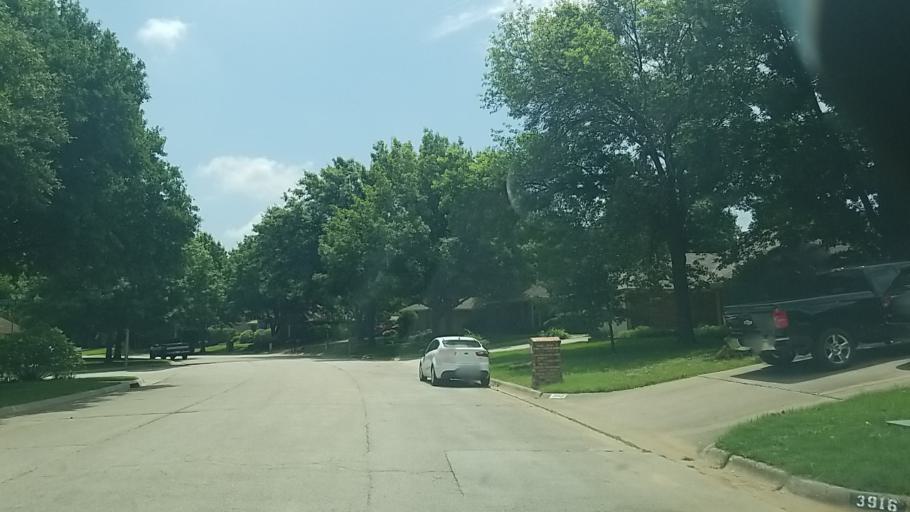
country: US
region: Texas
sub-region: Denton County
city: Corinth
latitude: 33.1640
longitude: -97.0875
